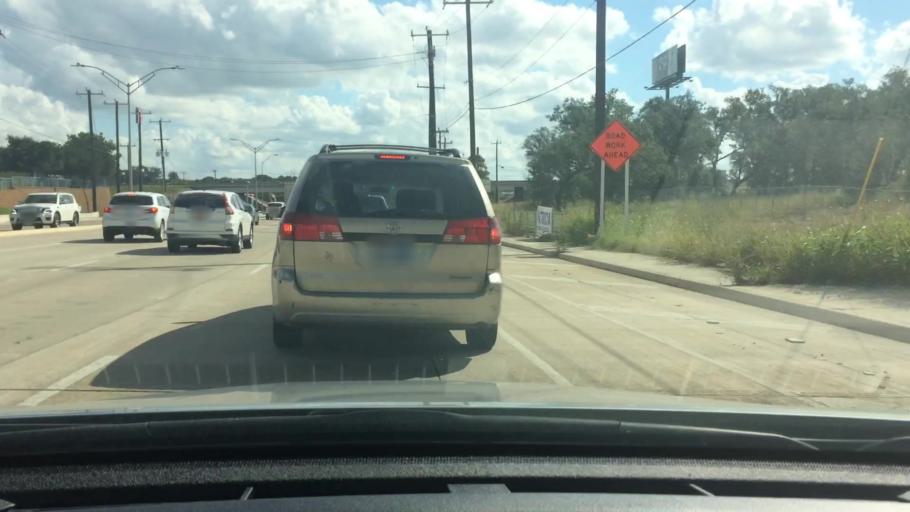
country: US
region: Texas
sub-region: Bexar County
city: Hollywood Park
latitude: 29.6028
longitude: -98.4188
